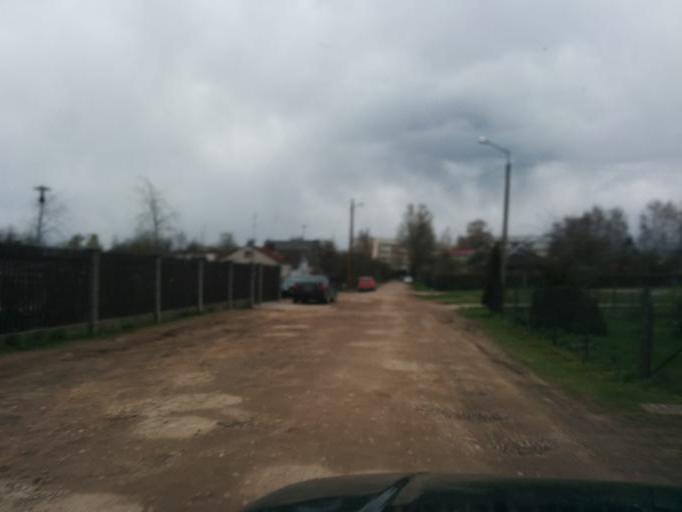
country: LV
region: Ozolnieku
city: Ozolnieki
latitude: 56.6579
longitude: 23.7579
